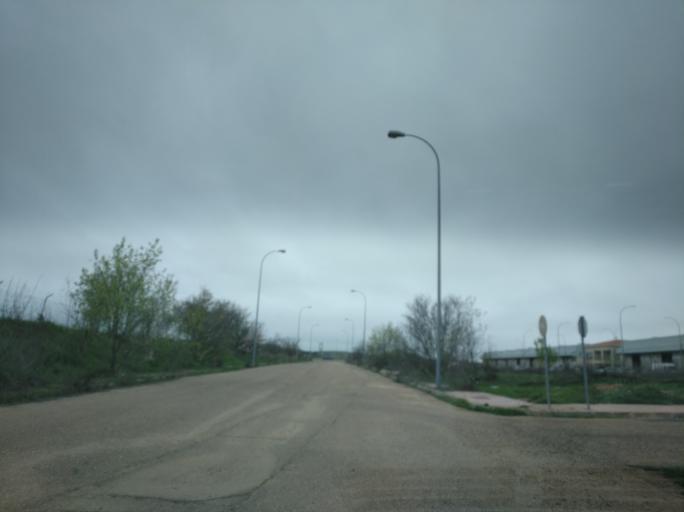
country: ES
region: Extremadura
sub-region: Provincia de Badajoz
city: Badajoz
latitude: 38.8998
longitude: -6.9657
